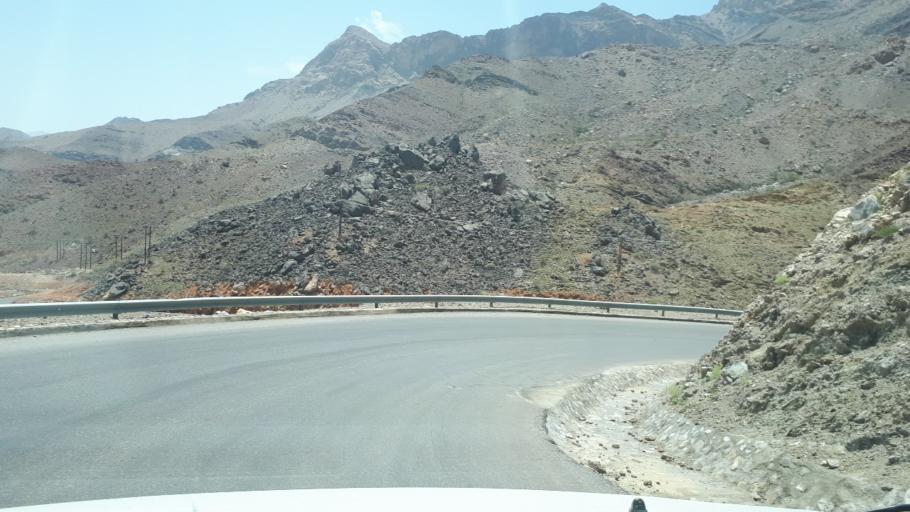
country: OM
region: Muhafazat ad Dakhiliyah
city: Bahla'
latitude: 23.1970
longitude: 57.1381
